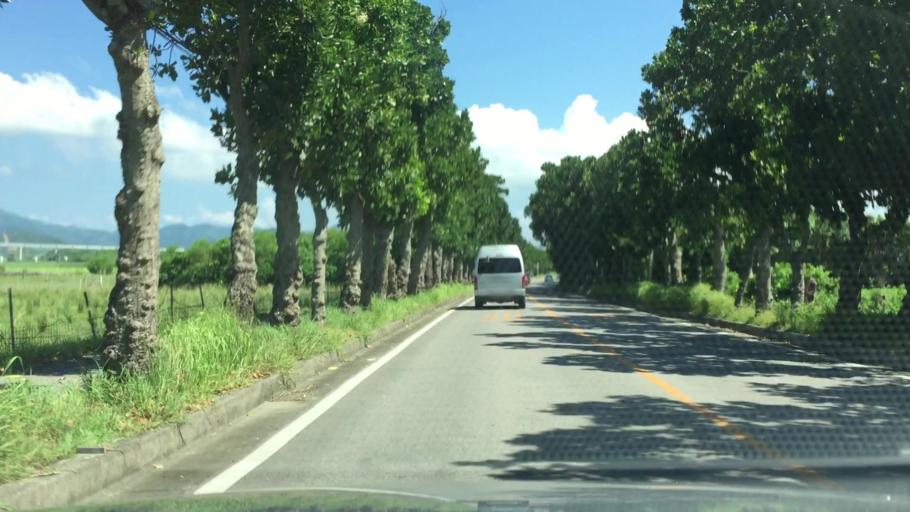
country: JP
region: Okinawa
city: Ishigaki
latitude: 24.3700
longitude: 124.2463
